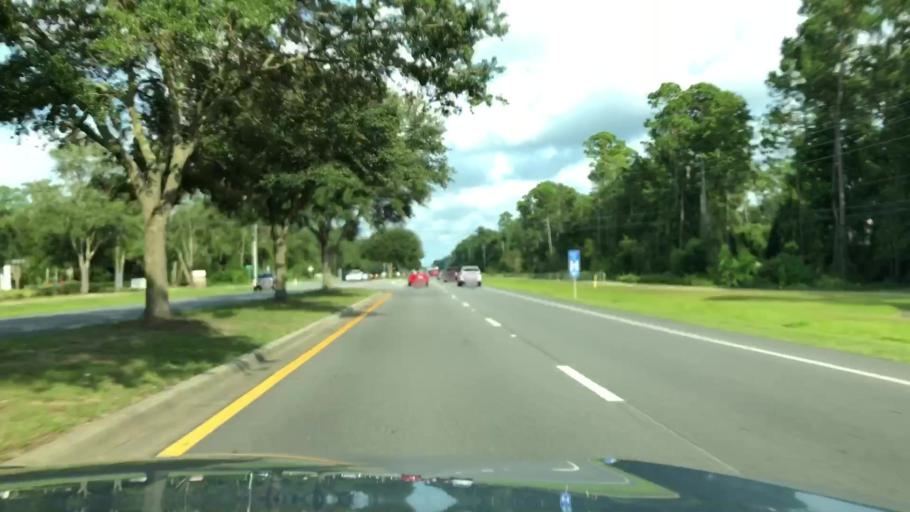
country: US
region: Florida
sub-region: Saint Johns County
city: Fruit Cove
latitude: 30.1095
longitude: -81.5665
